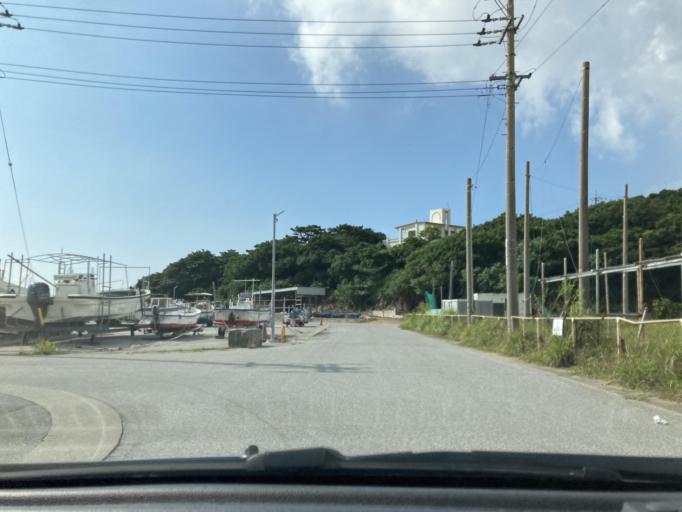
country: JP
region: Okinawa
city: Itoman
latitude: 26.1304
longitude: 127.7753
